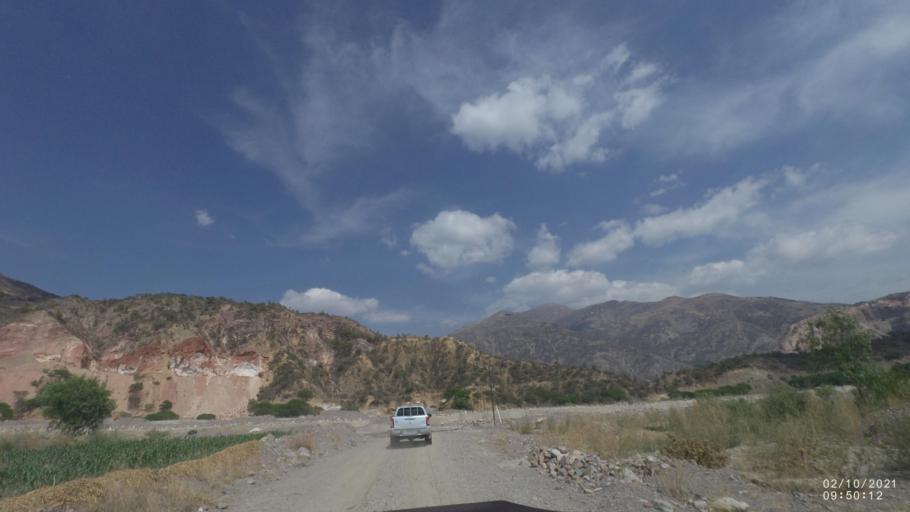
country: BO
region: Cochabamba
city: Irpa Irpa
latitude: -17.8011
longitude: -66.3370
